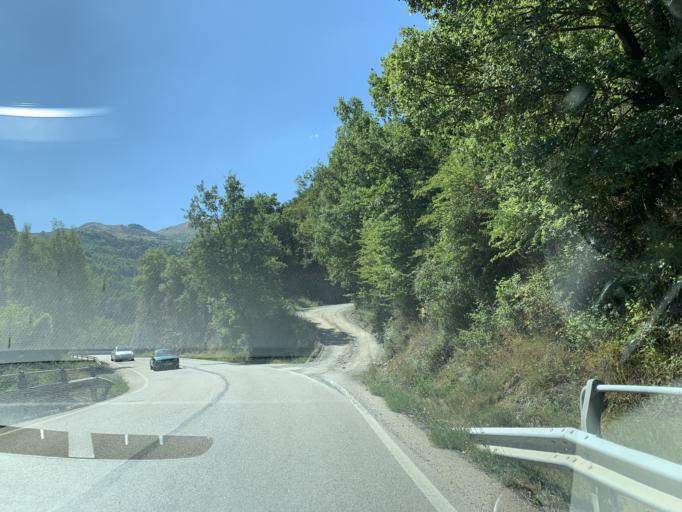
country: ES
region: Aragon
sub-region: Provincia de Huesca
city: Hoz de Jaca
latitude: 42.7300
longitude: -0.3034
